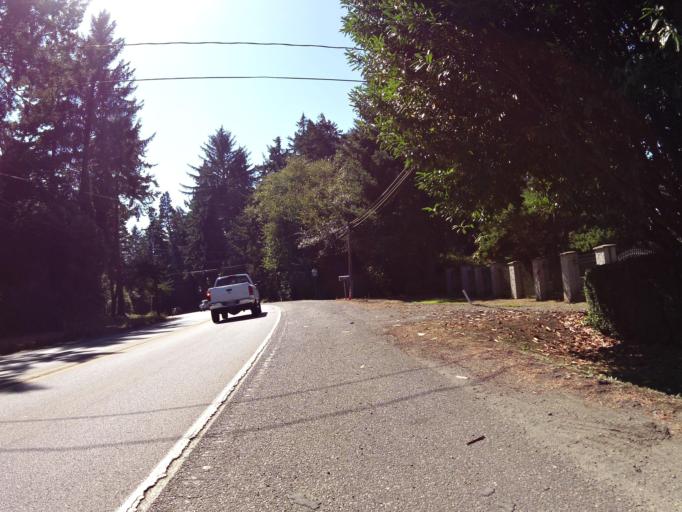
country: US
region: Oregon
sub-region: Coos County
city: Barview
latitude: 43.3471
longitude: -124.3152
